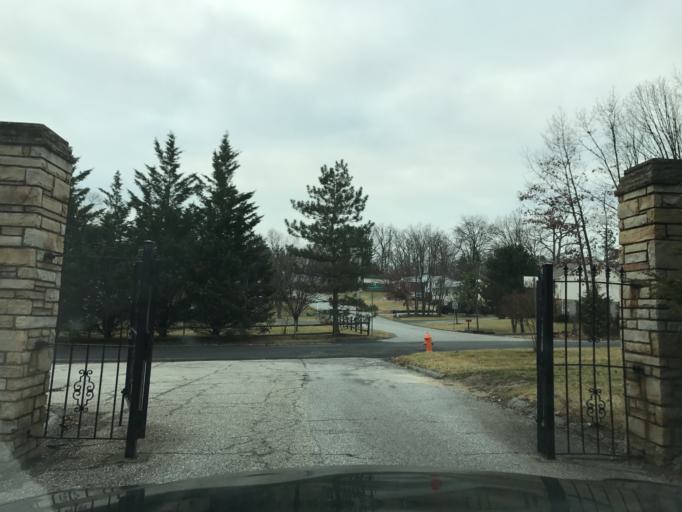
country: US
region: Maryland
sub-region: Baltimore County
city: Overlea
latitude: 39.3534
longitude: -76.5083
